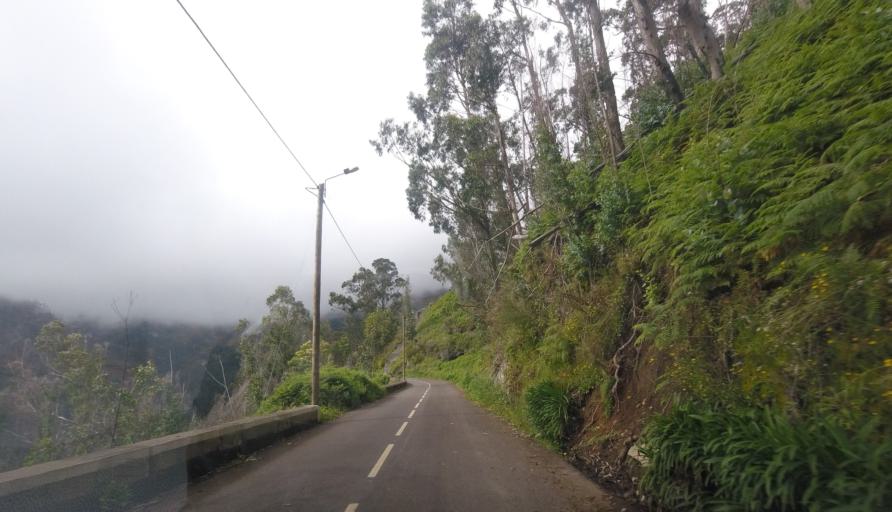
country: PT
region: Madeira
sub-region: Funchal
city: Nossa Senhora do Monte
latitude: 32.6836
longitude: -16.8913
